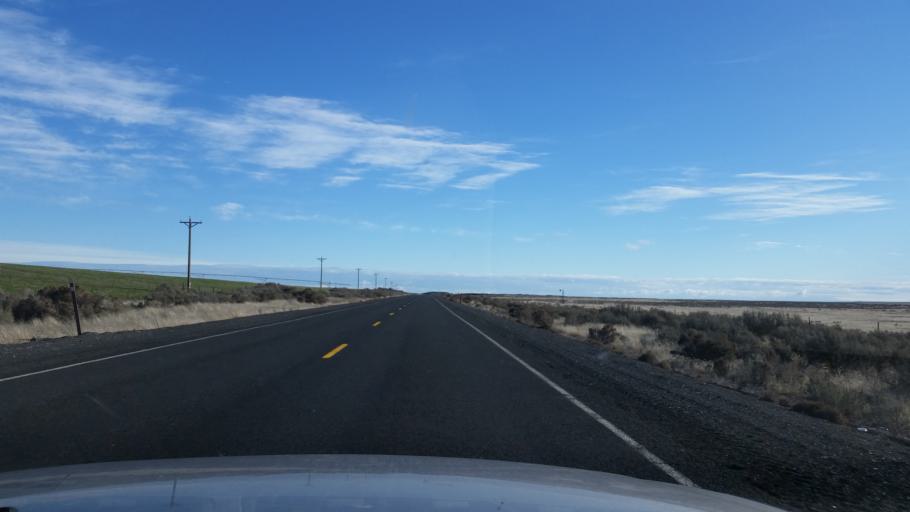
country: US
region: Washington
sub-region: Grant County
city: Warden
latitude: 47.3353
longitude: -118.8930
